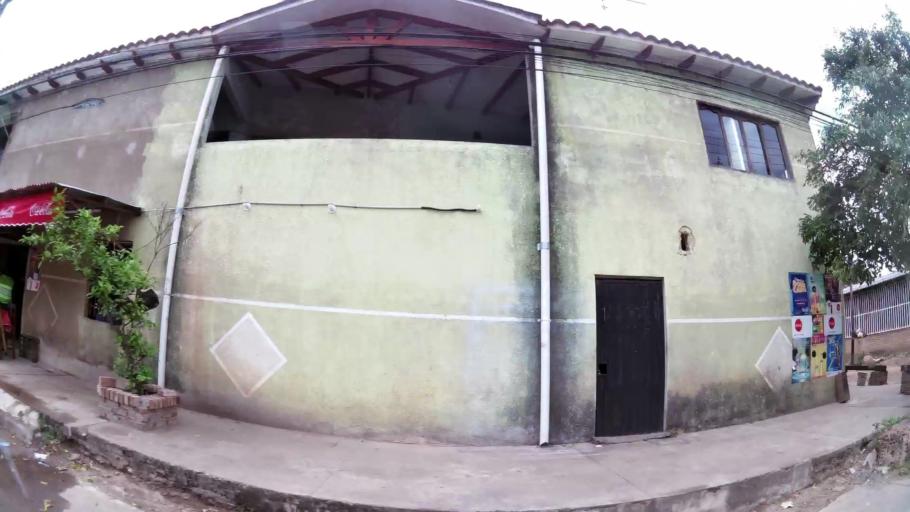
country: BO
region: Santa Cruz
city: Santa Cruz de la Sierra
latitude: -17.7418
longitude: -63.1757
